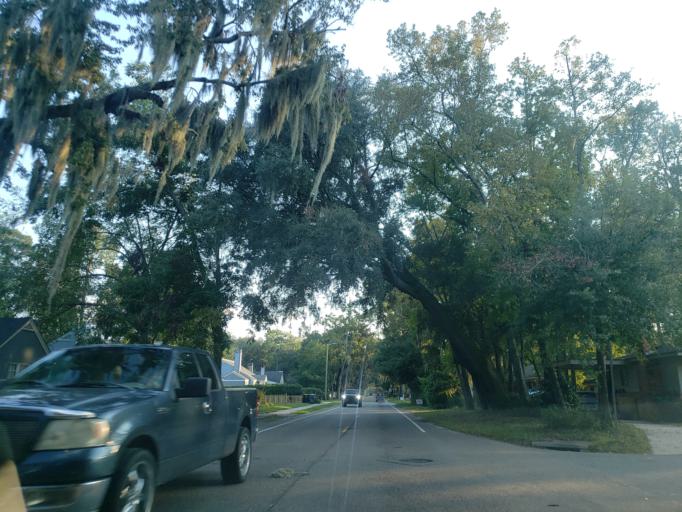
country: US
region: Georgia
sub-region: Chatham County
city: Thunderbolt
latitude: 32.0489
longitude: -81.0756
